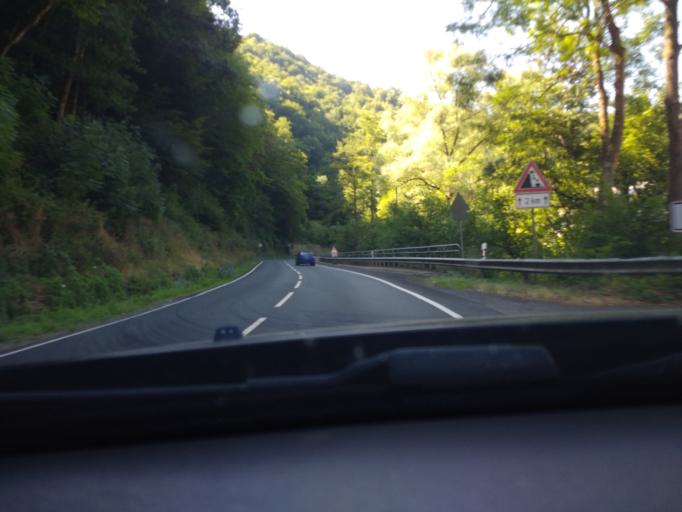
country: DE
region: Rheinland-Pfalz
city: Alf
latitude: 50.0568
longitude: 7.1041
